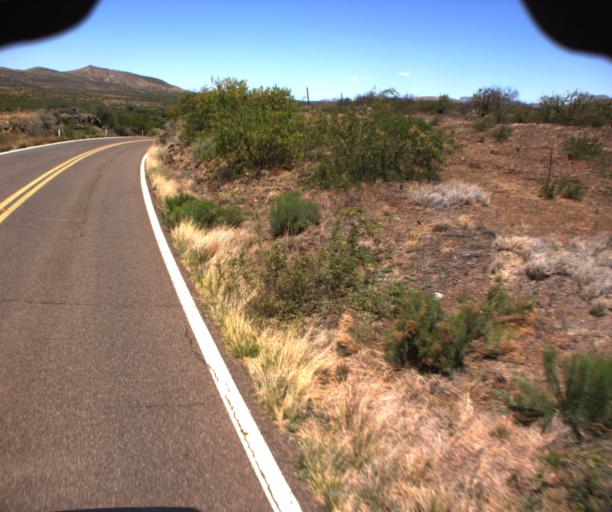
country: US
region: Arizona
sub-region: Cochise County
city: Douglas
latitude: 31.4594
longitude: -109.3779
